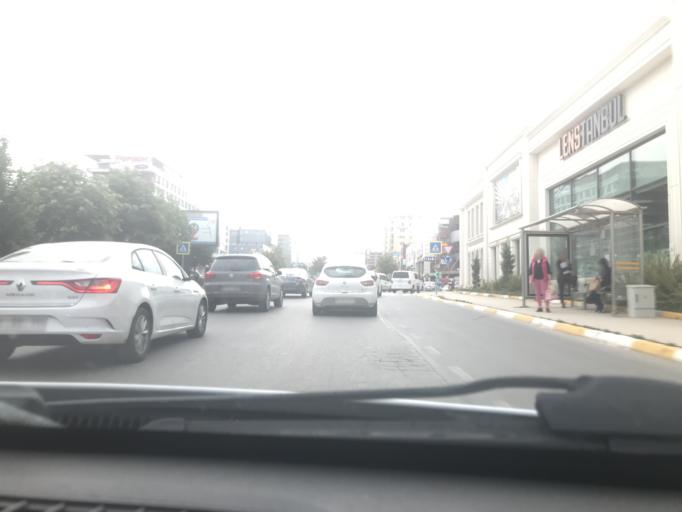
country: TR
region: Istanbul
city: Sultanbeyli
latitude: 40.9267
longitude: 29.3109
